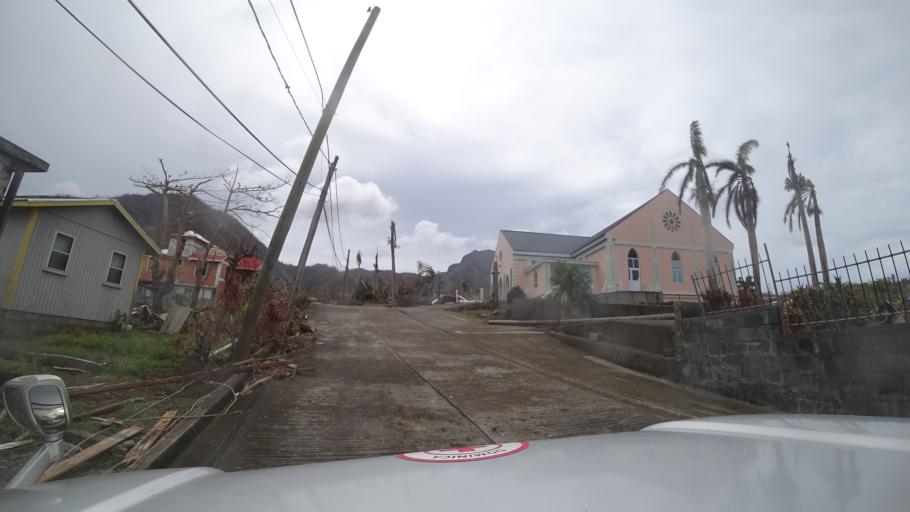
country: DM
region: Saint Andrew
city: Calibishie
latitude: 15.6142
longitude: -61.4065
